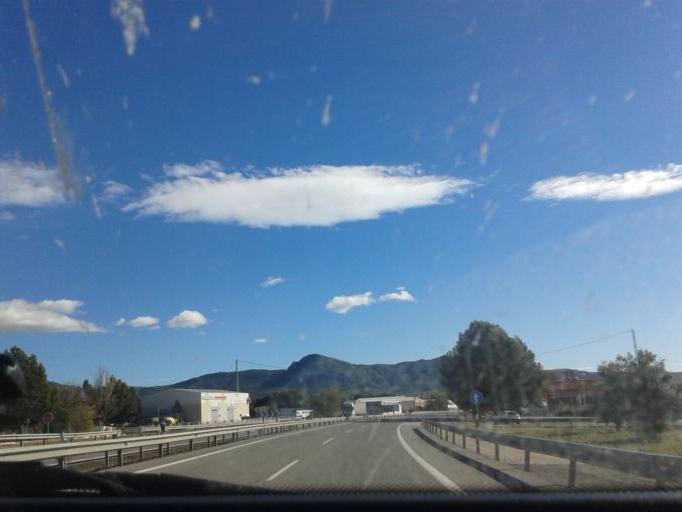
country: ES
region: Valencia
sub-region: Provincia de Alicante
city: Villena
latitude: 38.6249
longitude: -0.8532
